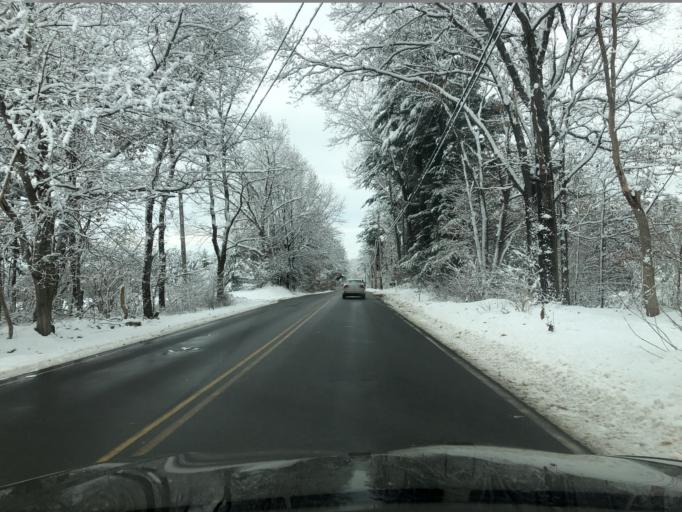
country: US
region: New Hampshire
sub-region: Strafford County
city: Somersworth
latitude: 43.2335
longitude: -70.8631
